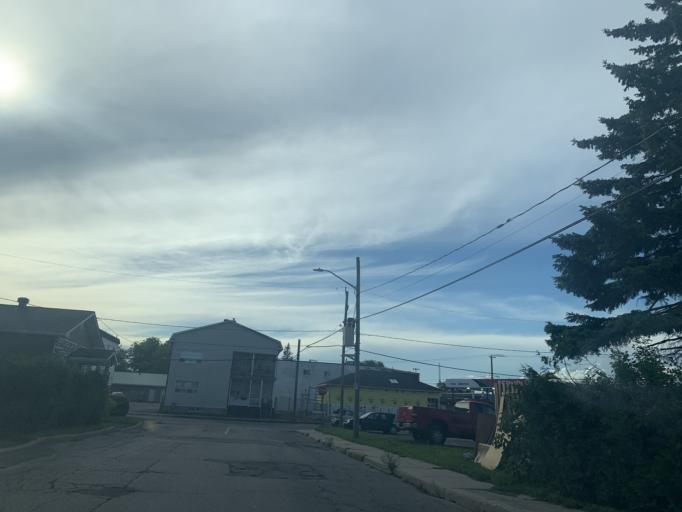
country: CA
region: Ontario
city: Hawkesbury
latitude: 45.6100
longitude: -74.5970
